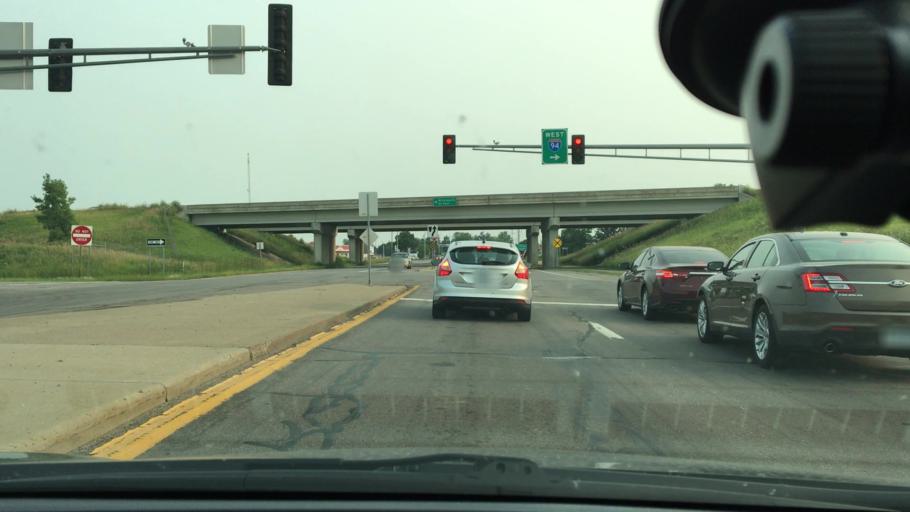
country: US
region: Minnesota
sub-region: Wright County
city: Albertville
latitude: 45.2423
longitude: -93.6634
